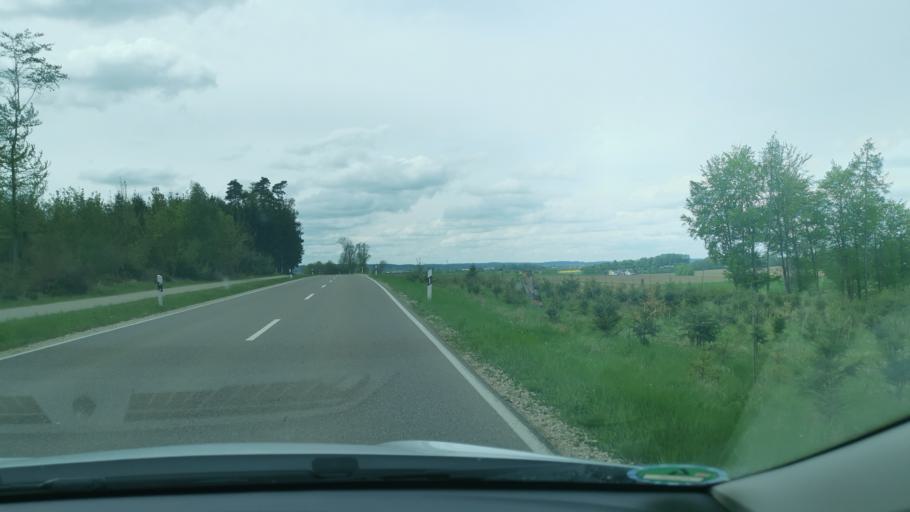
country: DE
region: Bavaria
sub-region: Swabia
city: Aichach
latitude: 48.4537
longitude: 11.1721
